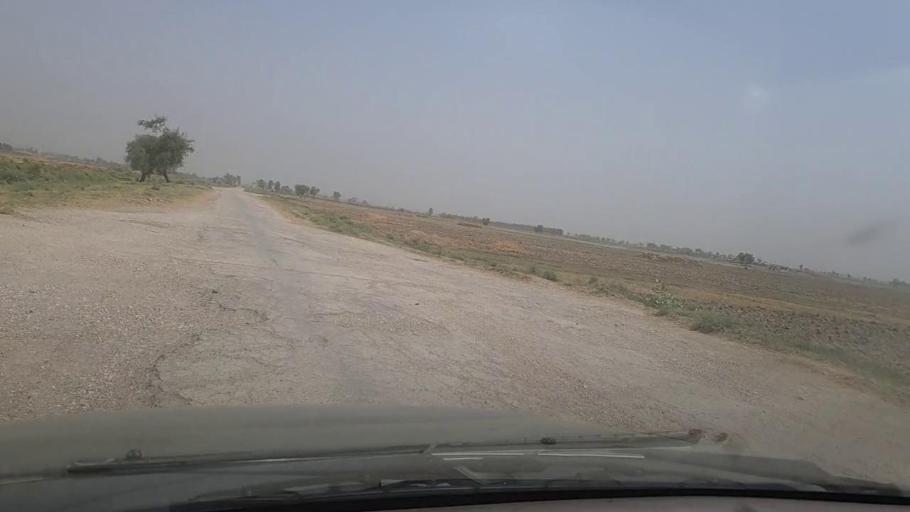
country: PK
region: Sindh
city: Madeji
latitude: 27.8109
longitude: 68.3978
